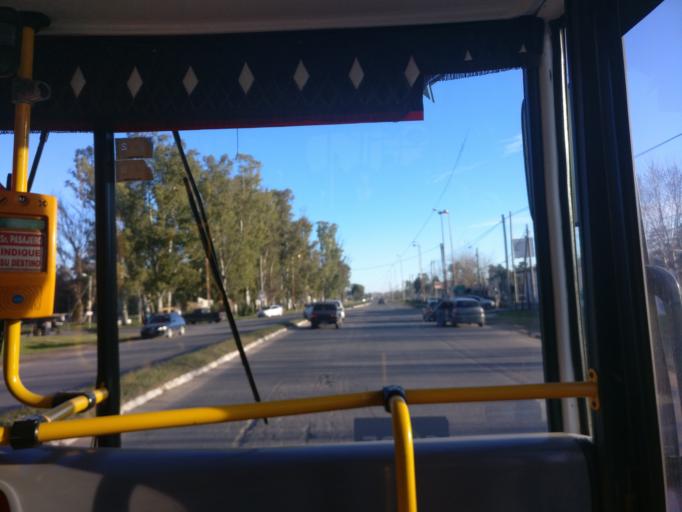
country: AR
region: Buenos Aires
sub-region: Partido de Ezeiza
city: Ezeiza
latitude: -34.9361
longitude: -58.6199
